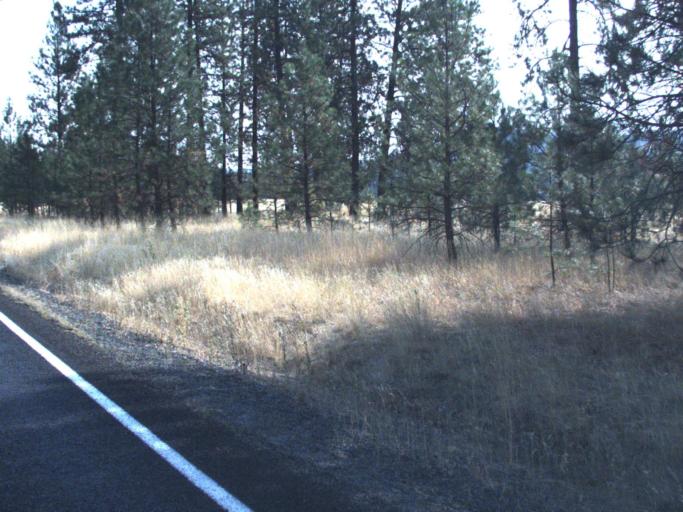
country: US
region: Washington
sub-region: Spokane County
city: Fairchild Air Force Base
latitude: 47.8439
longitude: -117.7352
